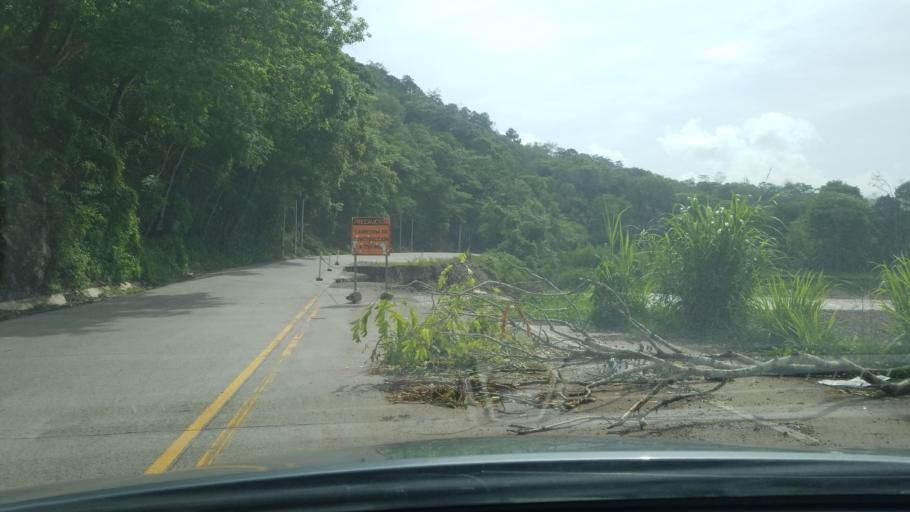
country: HN
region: Copan
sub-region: Santa Rita
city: Santa Rita, Copan
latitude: 14.8699
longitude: -89.0661
